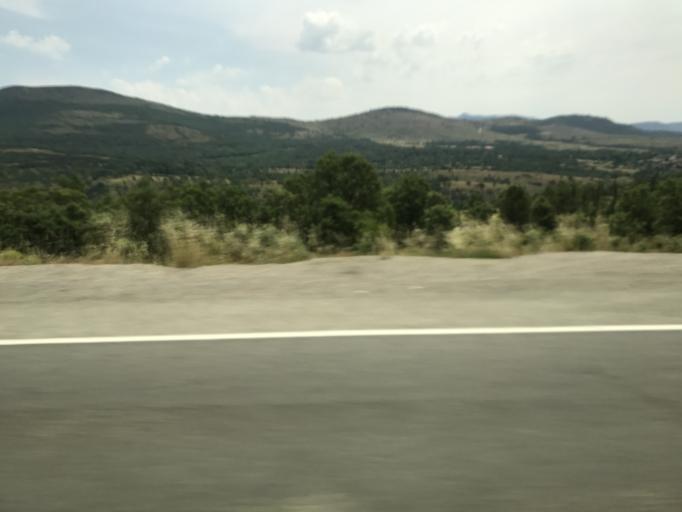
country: ES
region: Madrid
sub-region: Provincia de Madrid
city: Horcajo de la Sierra
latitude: 41.0828
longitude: -3.5980
